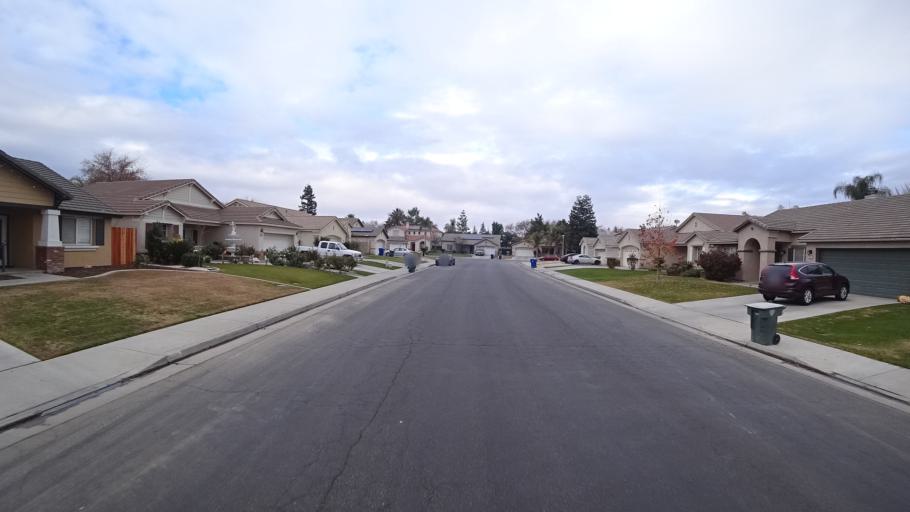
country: US
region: California
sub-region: Kern County
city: Greenfield
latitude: 35.3023
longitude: -119.0793
